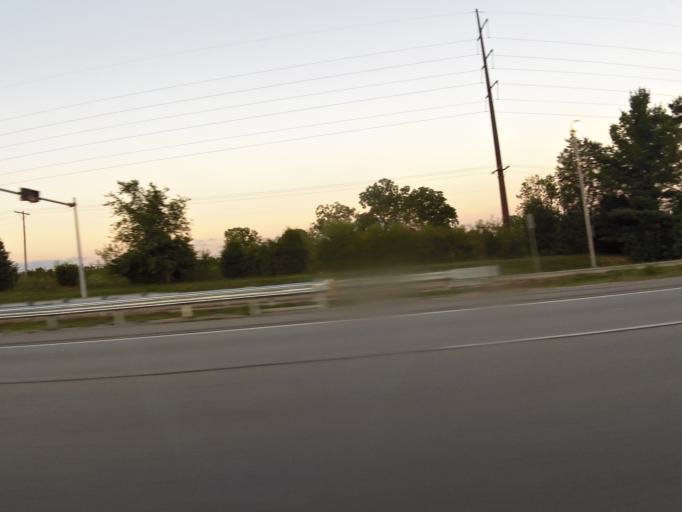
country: US
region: Kentucky
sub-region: Scott County
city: Georgetown
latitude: 38.2915
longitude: -84.5587
